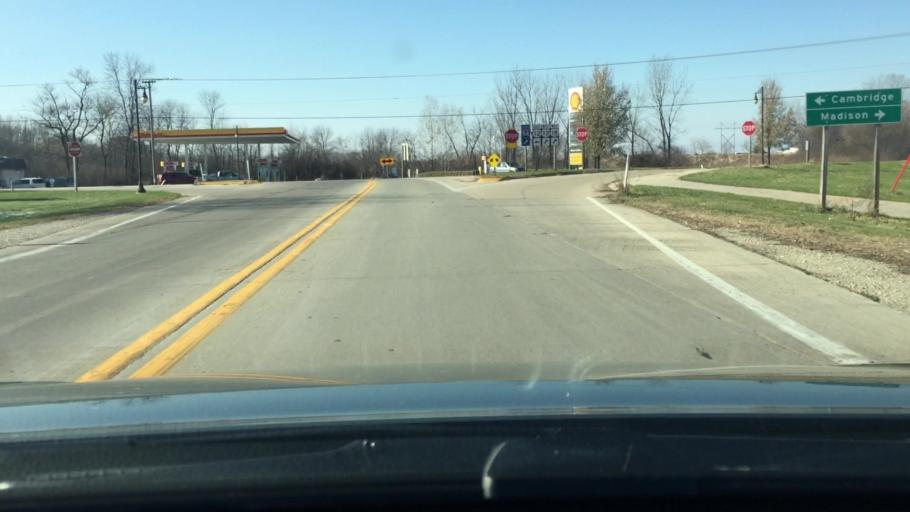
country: US
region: Wisconsin
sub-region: Jefferson County
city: Cambridge
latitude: 43.0088
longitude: -89.0217
